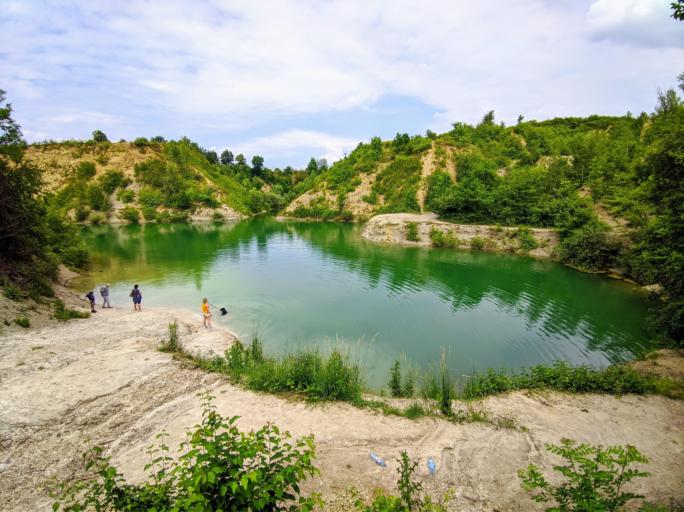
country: PL
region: Lower Silesian Voivodeship
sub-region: Powiat zlotoryjski
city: Olszanica
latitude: 51.1995
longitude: 15.6990
